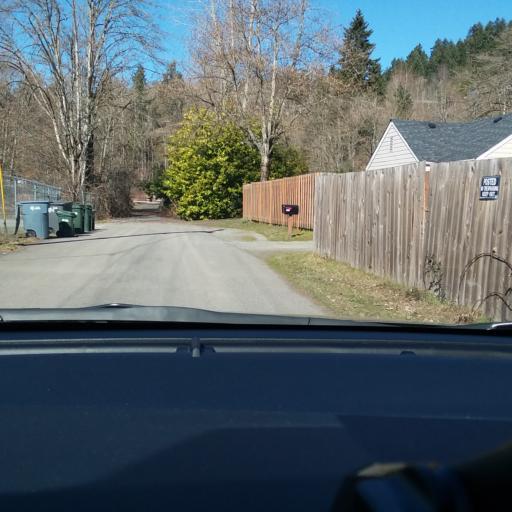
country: US
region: Washington
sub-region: Pierce County
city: North Puyallup
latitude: 47.2078
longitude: -122.2806
